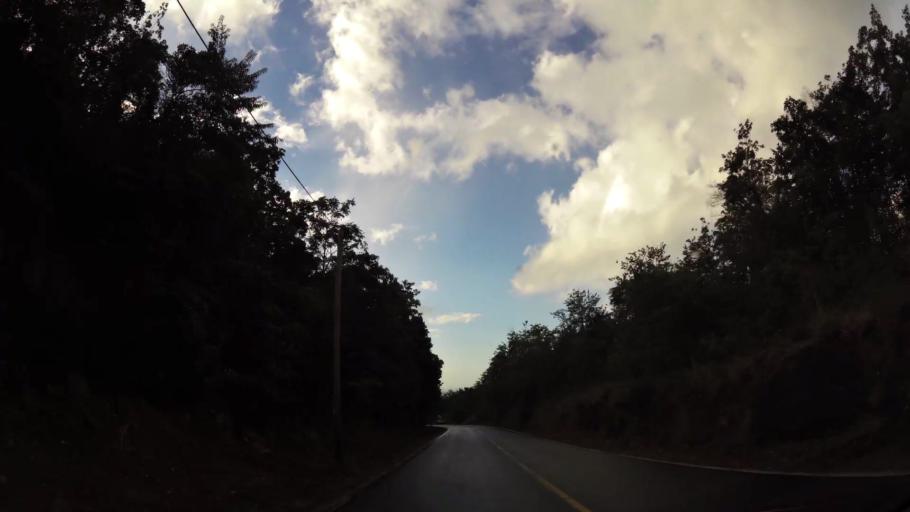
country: DM
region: Saint Peter
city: Colihaut
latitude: 15.5270
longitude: -61.4649
